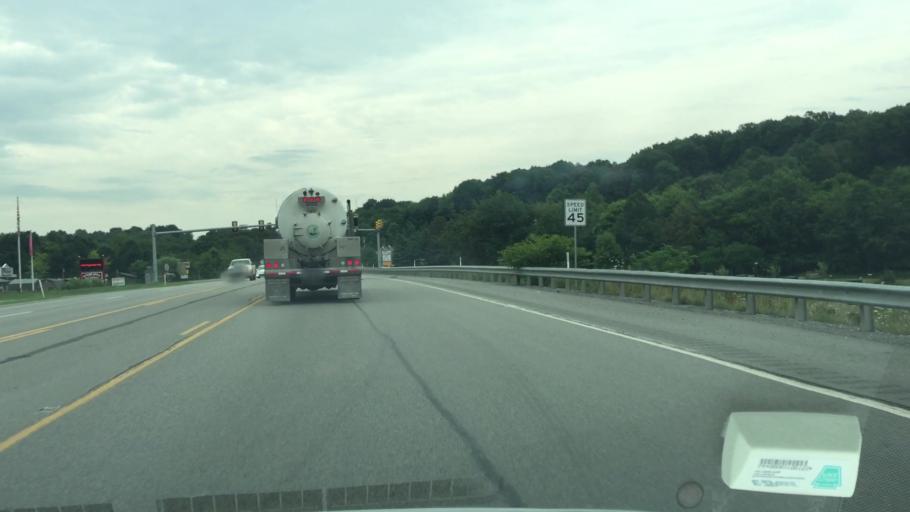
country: US
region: Pennsylvania
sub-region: Butler County
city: Mars
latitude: 40.6907
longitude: -80.0033
